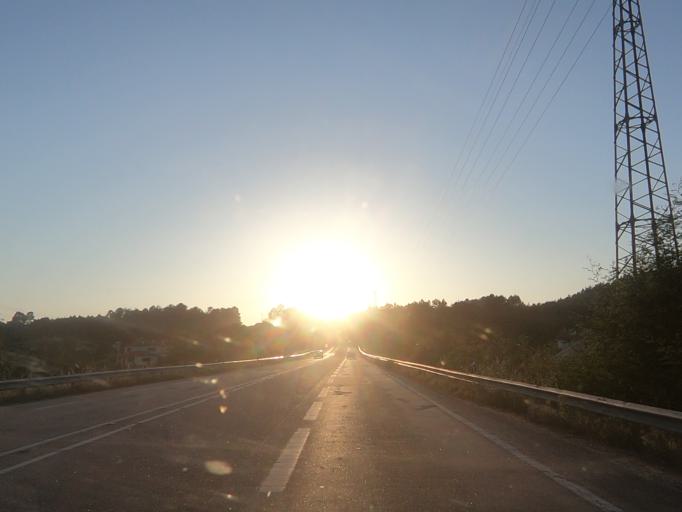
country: PT
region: Viseu
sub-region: Viseu
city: Rio de Loba
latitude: 40.6814
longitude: -7.8839
